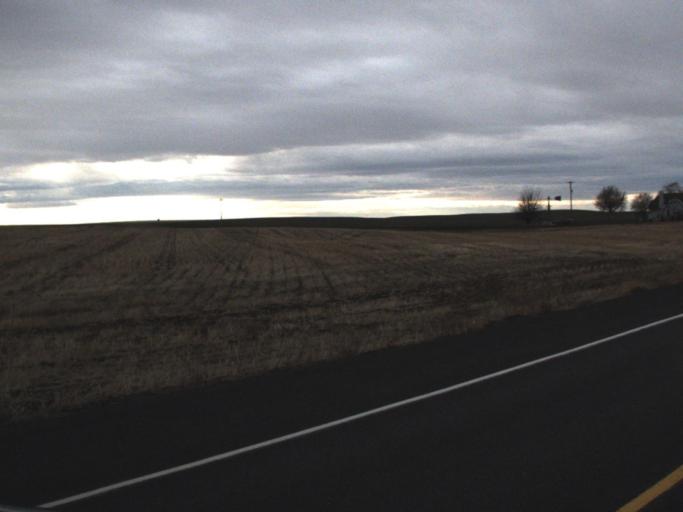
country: US
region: Washington
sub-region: Adams County
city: Ritzville
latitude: 46.7953
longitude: -118.3974
